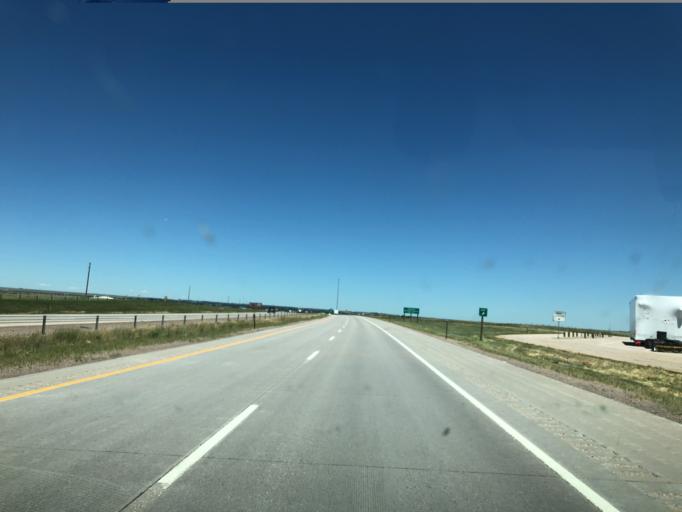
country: US
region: Wyoming
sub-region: Laramie County
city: South Greeley
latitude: 41.0823
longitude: -104.8542
